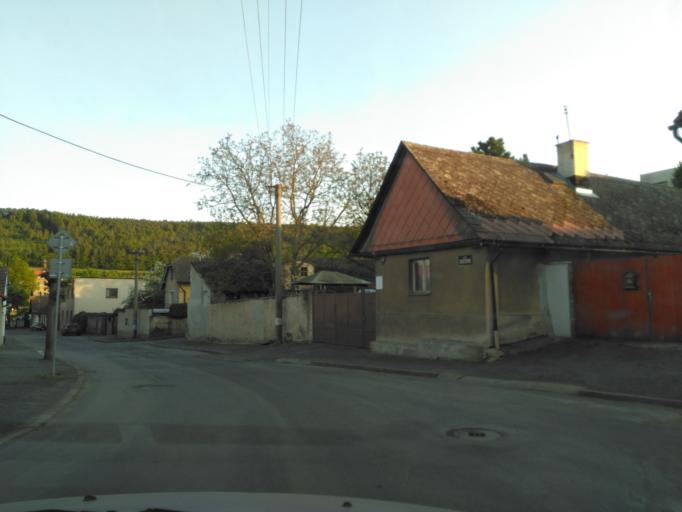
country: CZ
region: Central Bohemia
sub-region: Okres Beroun
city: Kraluv Dvur
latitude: 49.9067
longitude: 14.0335
